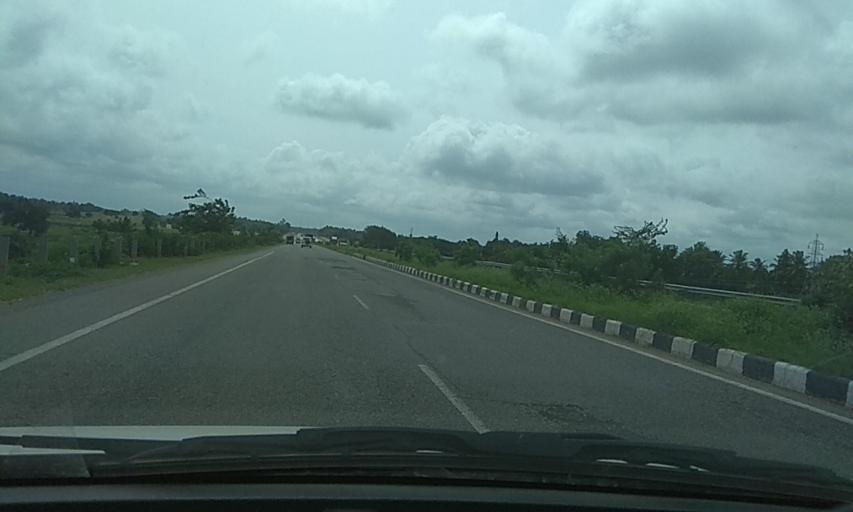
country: IN
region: Karnataka
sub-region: Davanagere
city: Mayakonda
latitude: 14.4044
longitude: 76.0022
